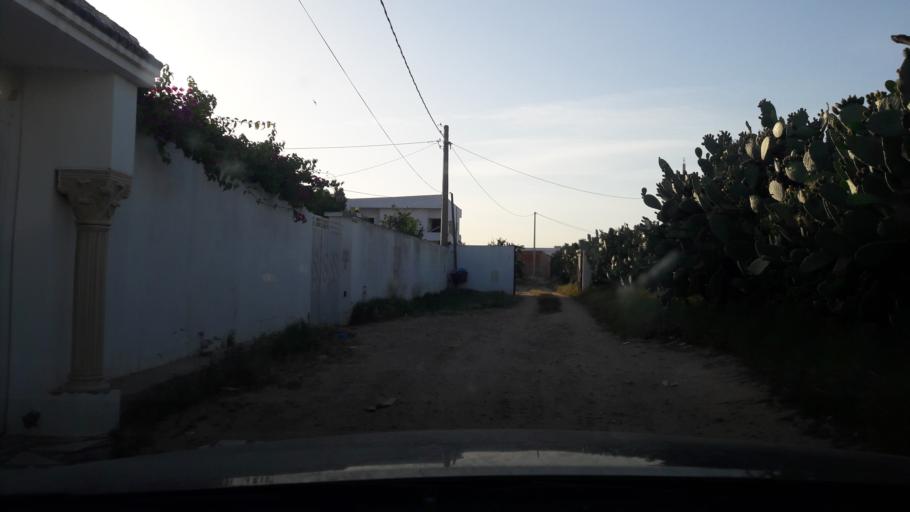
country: TN
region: Safaqis
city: Sfax
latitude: 34.7946
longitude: 10.7515
